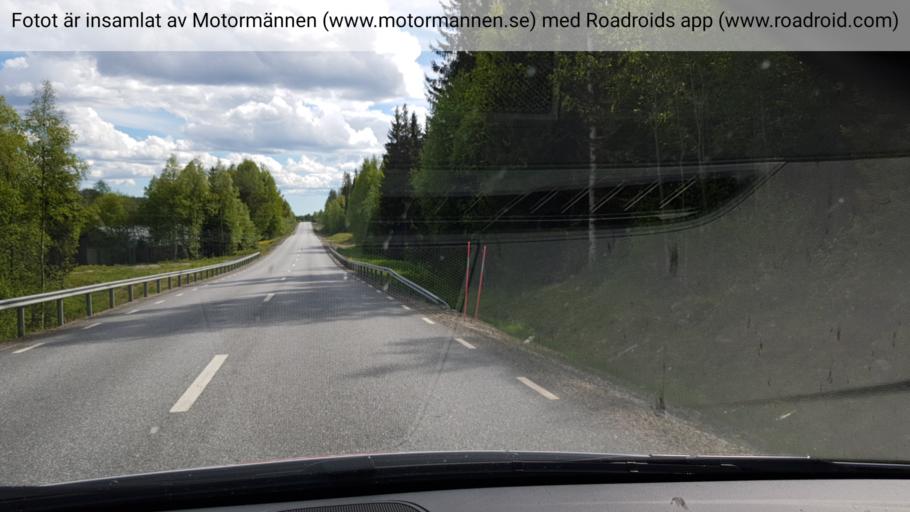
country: SE
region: Vaesterbotten
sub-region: Umea Kommun
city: Ersmark
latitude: 64.3045
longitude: 20.2218
